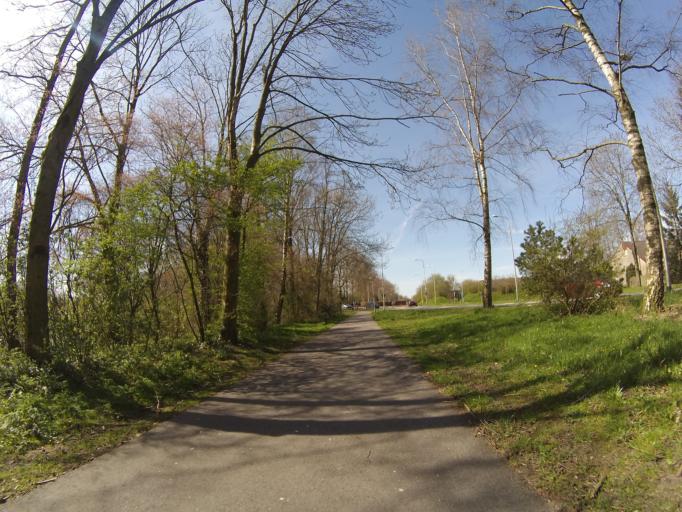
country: NL
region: Gelderland
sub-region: Gemeente Nijkerk
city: Nijkerk
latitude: 52.2108
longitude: 5.4884
